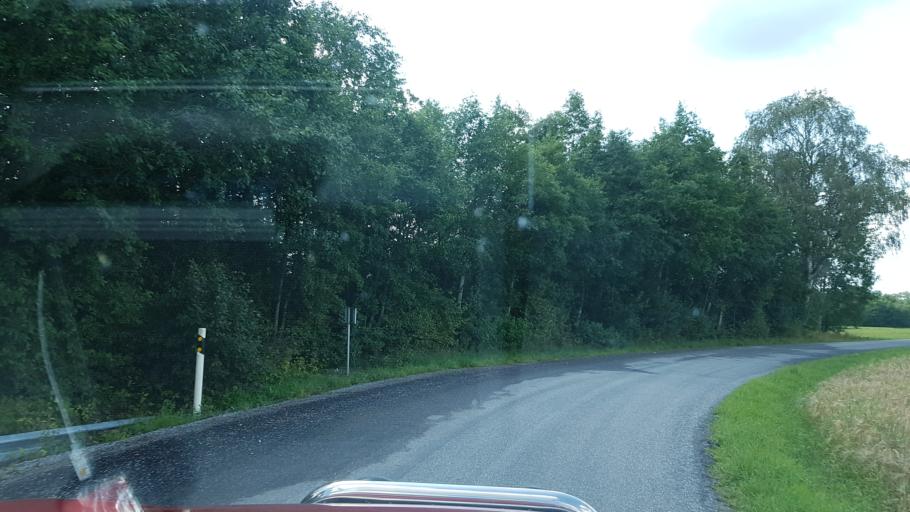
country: EE
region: Raplamaa
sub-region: Rapla vald
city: Rapla
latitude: 58.9345
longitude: 24.6374
